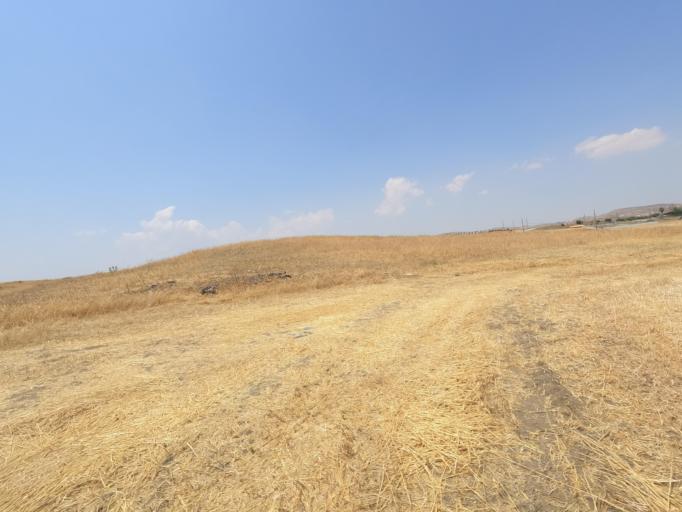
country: CY
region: Larnaka
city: Troulloi
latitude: 35.0124
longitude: 33.6085
